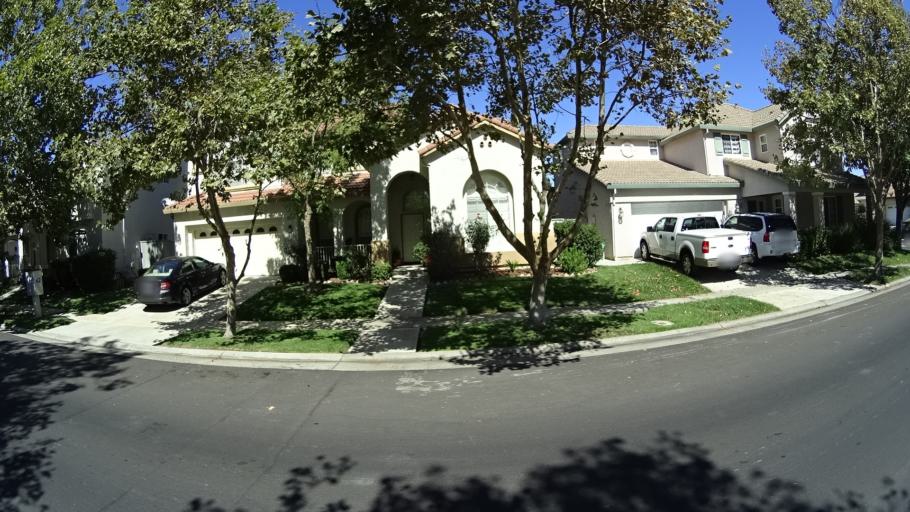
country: US
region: California
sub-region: Sacramento County
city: Laguna
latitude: 38.4172
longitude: -121.4765
